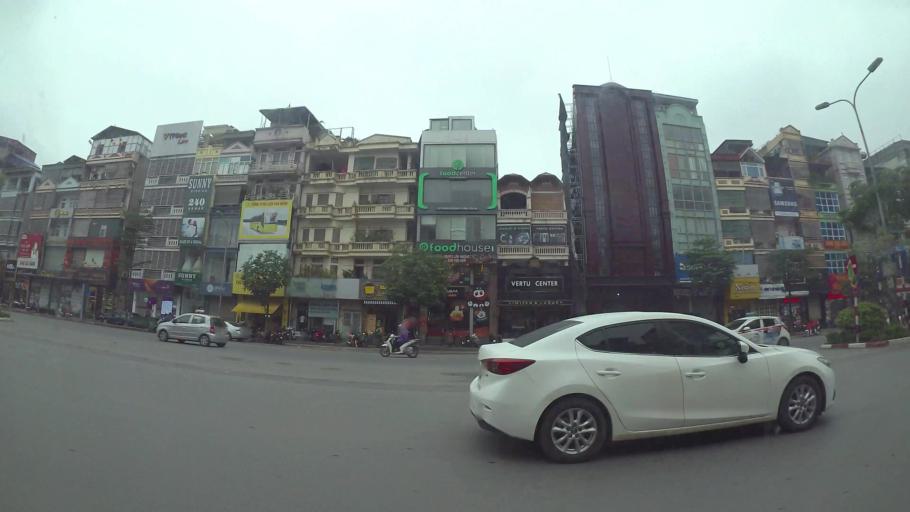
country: VN
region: Ha Noi
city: Dong Da
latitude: 21.0120
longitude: 105.8363
